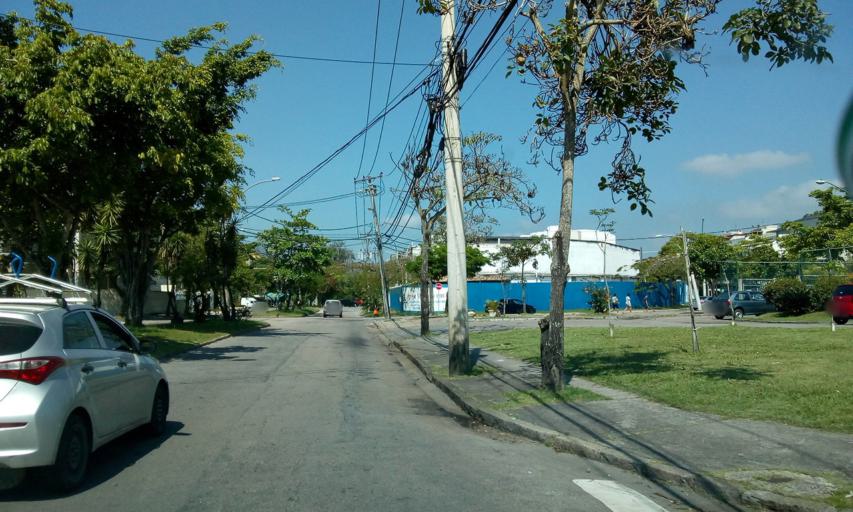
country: BR
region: Rio de Janeiro
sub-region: Nilopolis
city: Nilopolis
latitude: -23.0176
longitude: -43.4634
